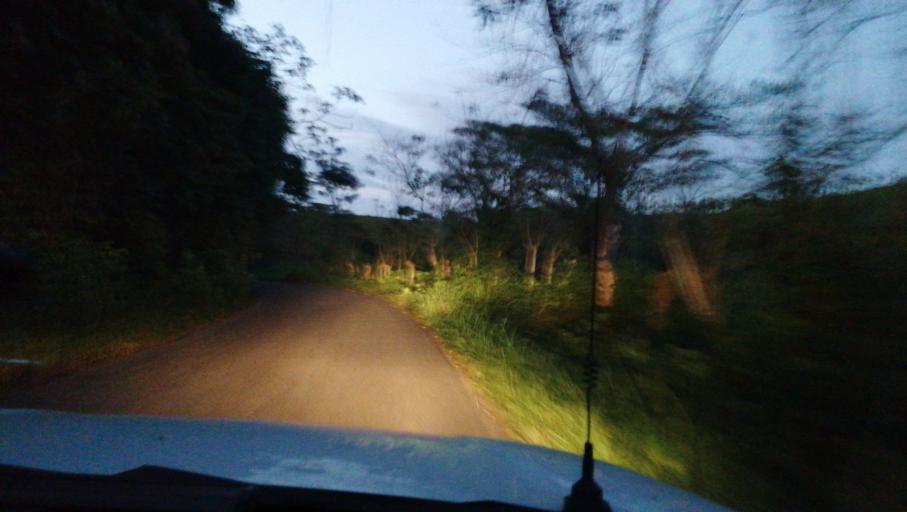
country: MX
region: Chiapas
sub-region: Ostuacan
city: Nuevo Juan del Grijalva
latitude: 17.4769
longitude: -93.3457
